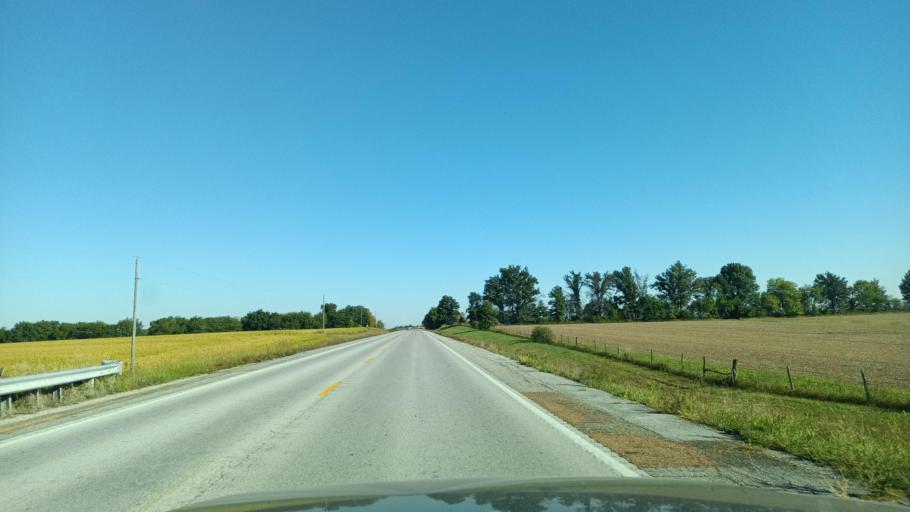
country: US
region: Missouri
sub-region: Audrain County
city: Vandalia
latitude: 39.3117
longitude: -91.6435
